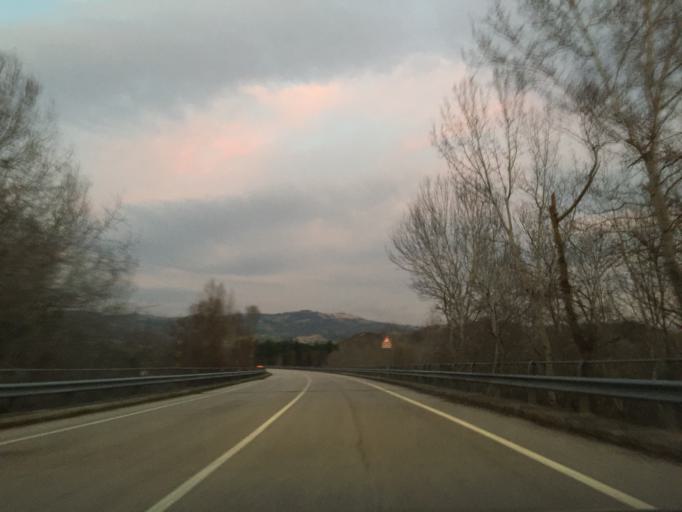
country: IT
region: Molise
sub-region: Provincia di Campobasso
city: Gambatesa
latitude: 41.5217
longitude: 14.9445
